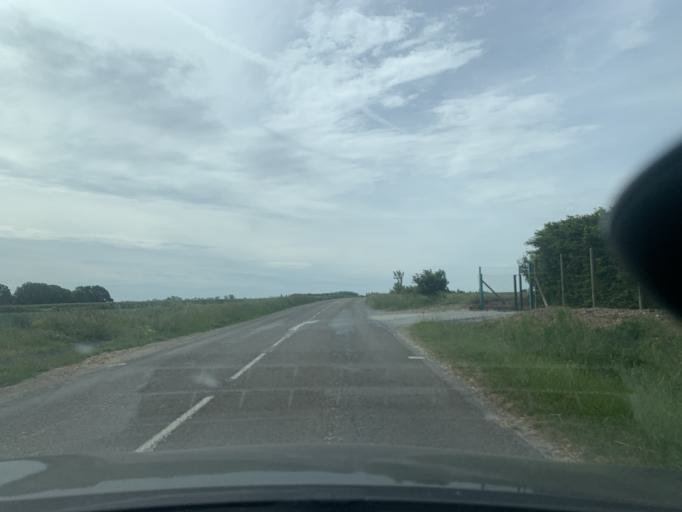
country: FR
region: Nord-Pas-de-Calais
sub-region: Departement du Nord
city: Marcoing
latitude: 50.1338
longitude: 3.1830
